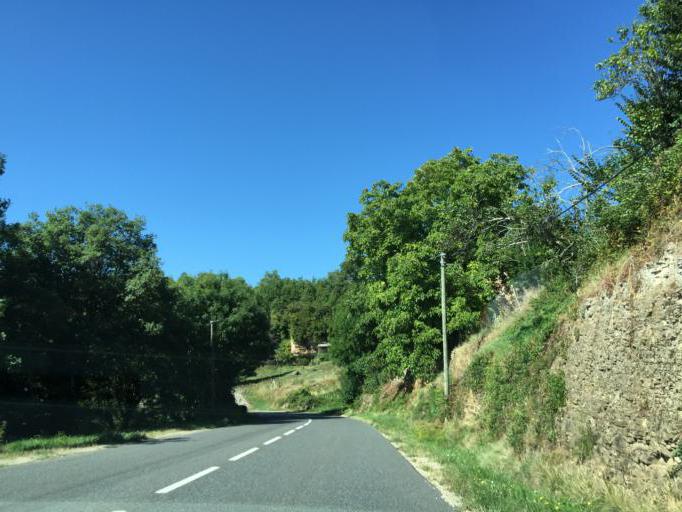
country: FR
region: Midi-Pyrenees
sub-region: Departement de l'Aveyron
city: Saint-Georges-de-Luzencon
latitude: 44.0820
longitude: 2.9013
